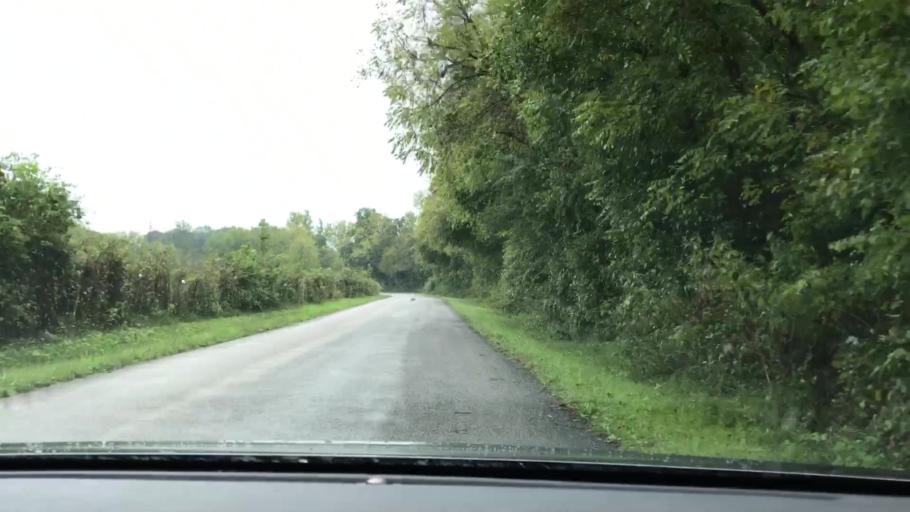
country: US
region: Tennessee
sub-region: Macon County
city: Red Boiling Springs
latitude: 36.5912
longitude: -85.7775
